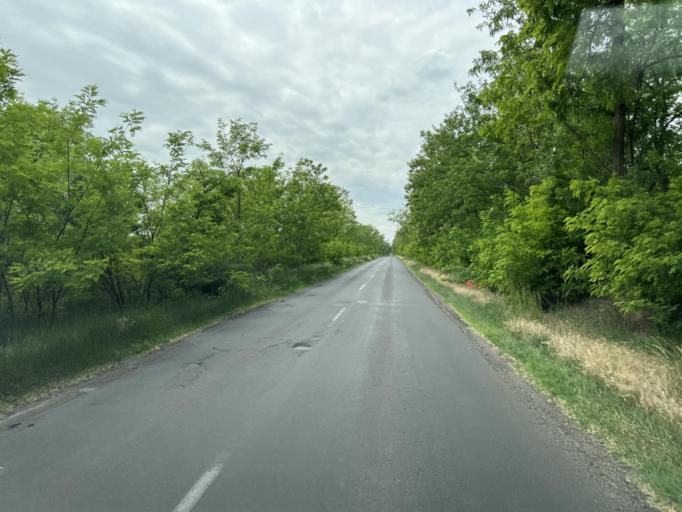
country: HU
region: Pest
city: Tapioszecso
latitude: 47.4691
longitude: 19.6181
